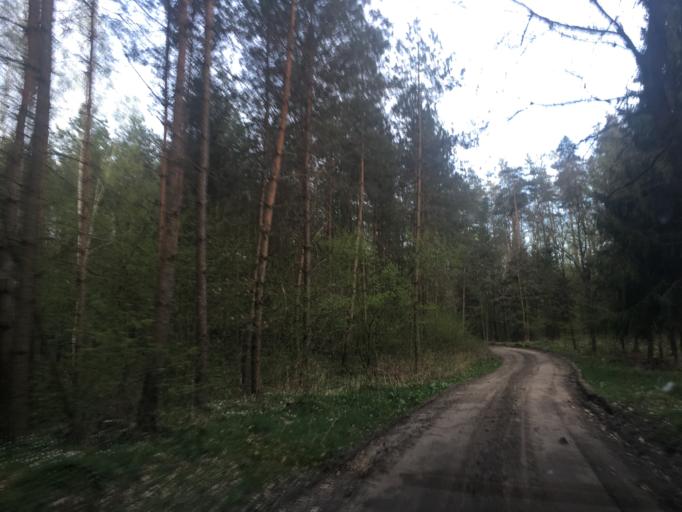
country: PL
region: Kujawsko-Pomorskie
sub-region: Powiat brodnicki
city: Gorzno
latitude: 53.2045
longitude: 19.6792
